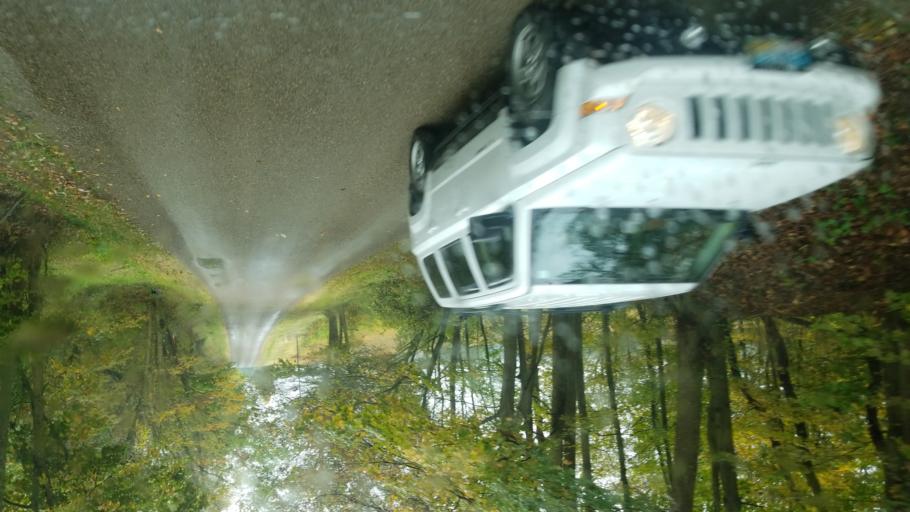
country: US
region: Ohio
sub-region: Sandusky County
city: Bellville
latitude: 40.6660
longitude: -82.3968
